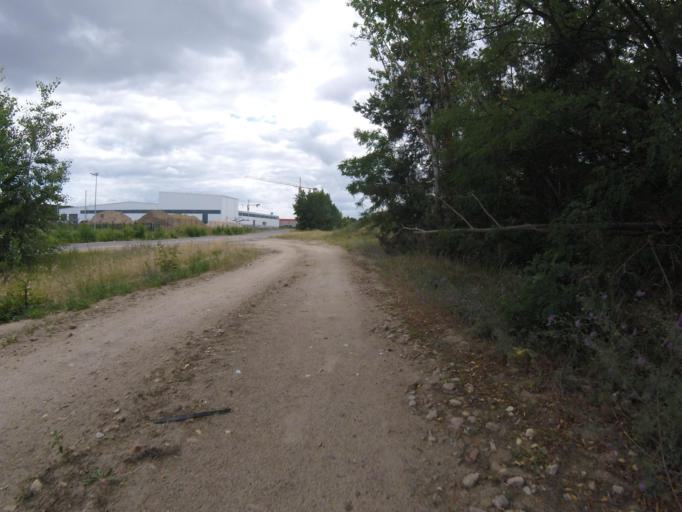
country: DE
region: Brandenburg
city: Wildau
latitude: 52.3233
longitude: 13.6745
